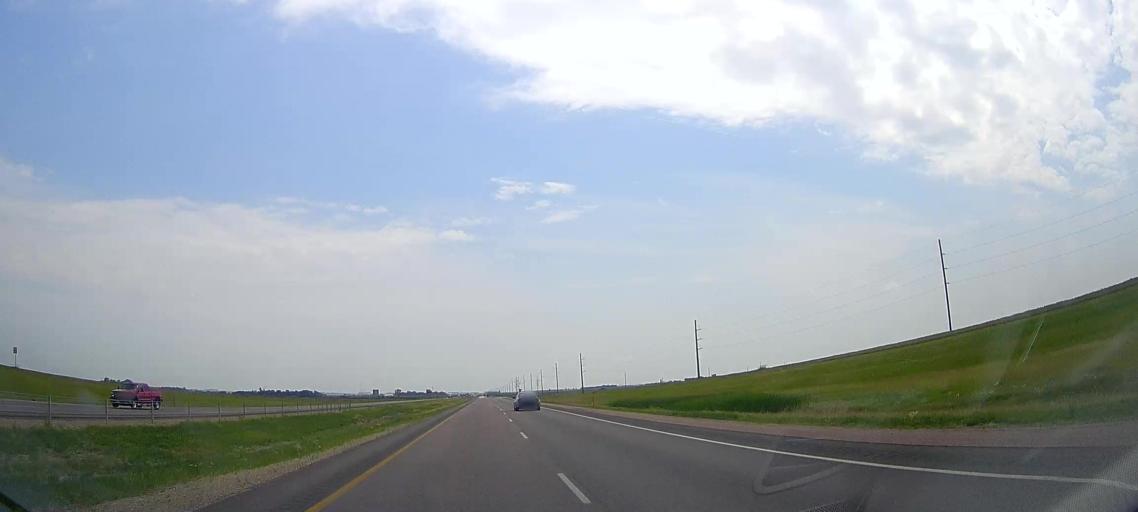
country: US
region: South Dakota
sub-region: Lincoln County
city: Lennox
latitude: 43.2567
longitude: -96.7961
